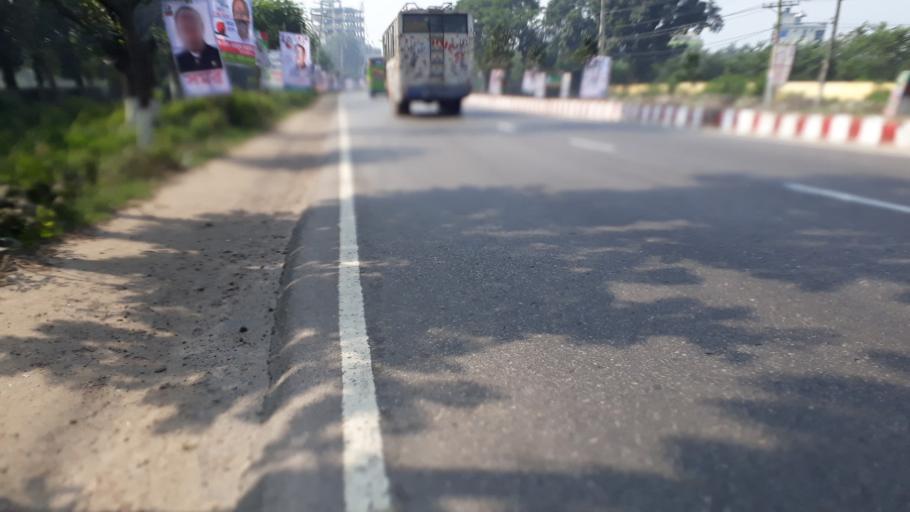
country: BD
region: Dhaka
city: Tungi
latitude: 23.8626
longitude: 90.2669
